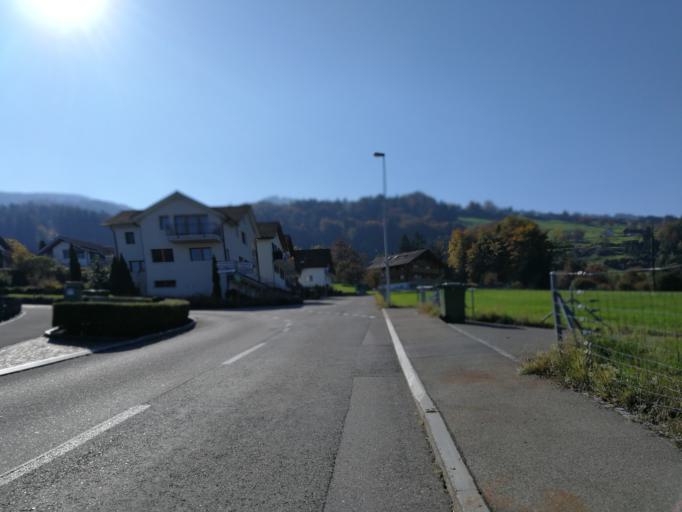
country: CH
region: Schwyz
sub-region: Bezirk March
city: Altendorf
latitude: 47.1863
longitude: 8.8273
